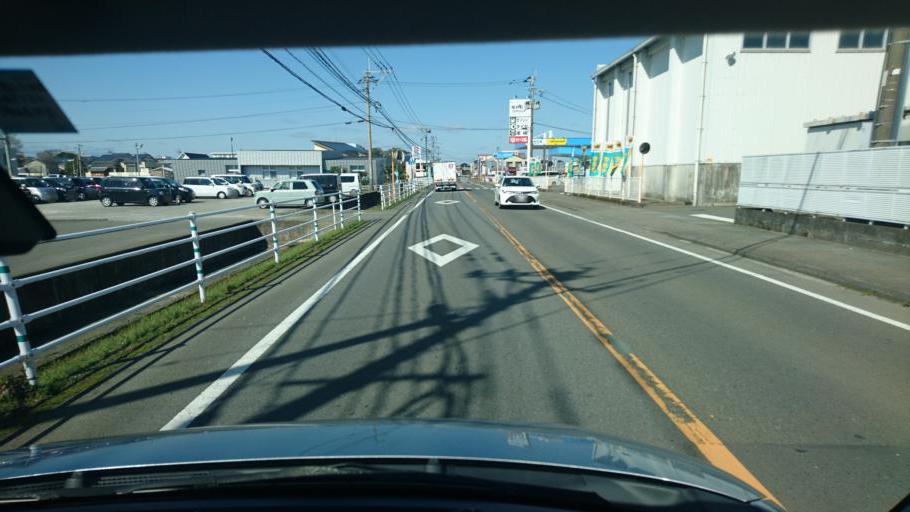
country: JP
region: Miyazaki
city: Miyazaki-shi
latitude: 31.8537
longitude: 131.4349
